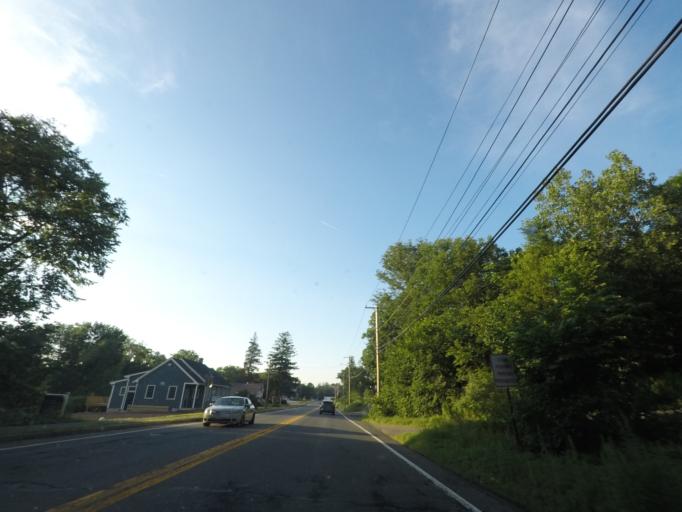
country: US
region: Massachusetts
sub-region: Hampden County
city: Brimfield
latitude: 42.1189
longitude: -72.1985
